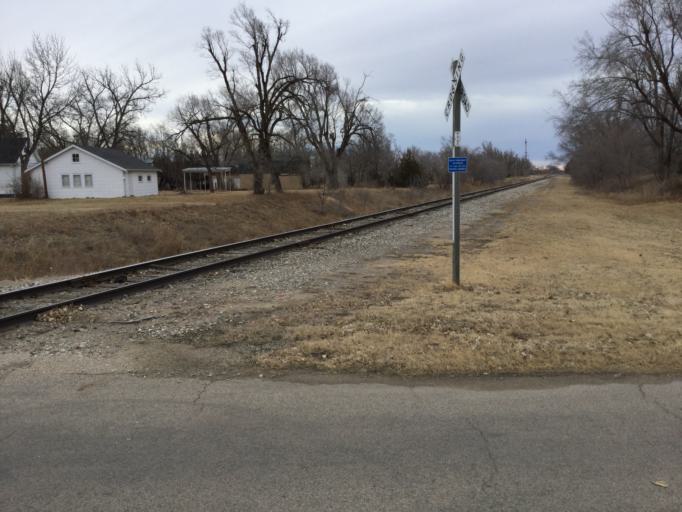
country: US
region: Kansas
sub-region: Rice County
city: Sterling
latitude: 38.2049
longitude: -98.2005
